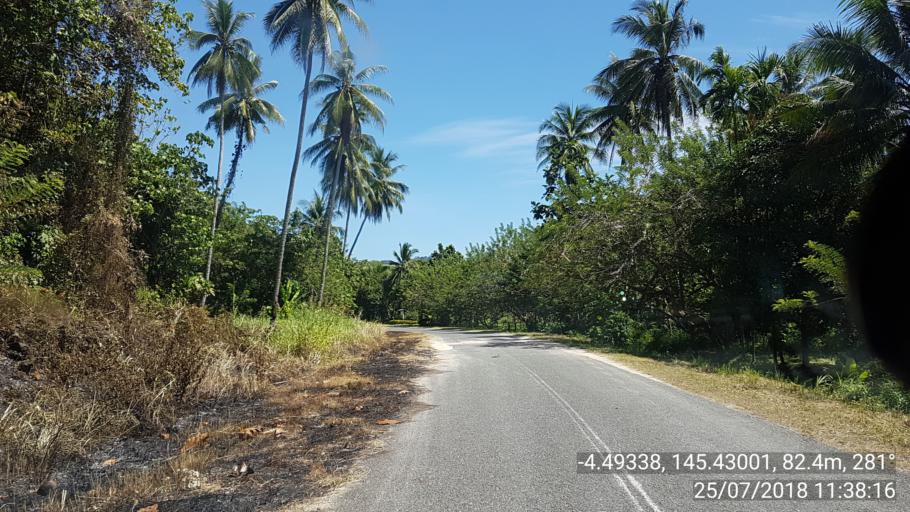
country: PG
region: Madang
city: Madang
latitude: -4.4933
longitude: 145.4300
